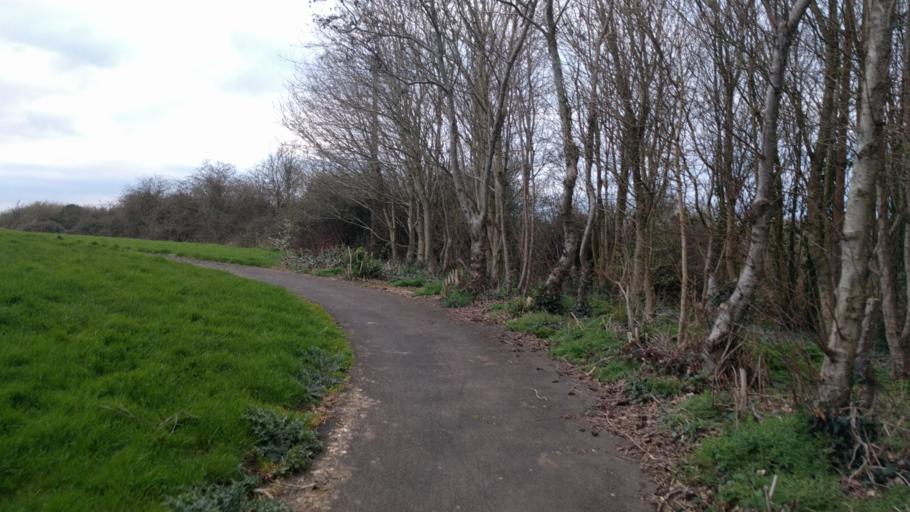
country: IE
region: Leinster
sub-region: Fingal County
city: Swords
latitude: 53.4559
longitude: -6.2292
